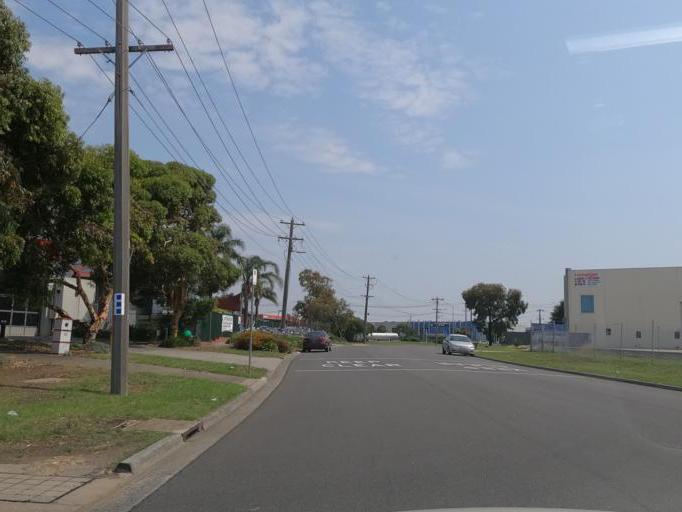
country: AU
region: Victoria
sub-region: Hume
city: Coolaroo
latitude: -37.6446
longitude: 144.9469
